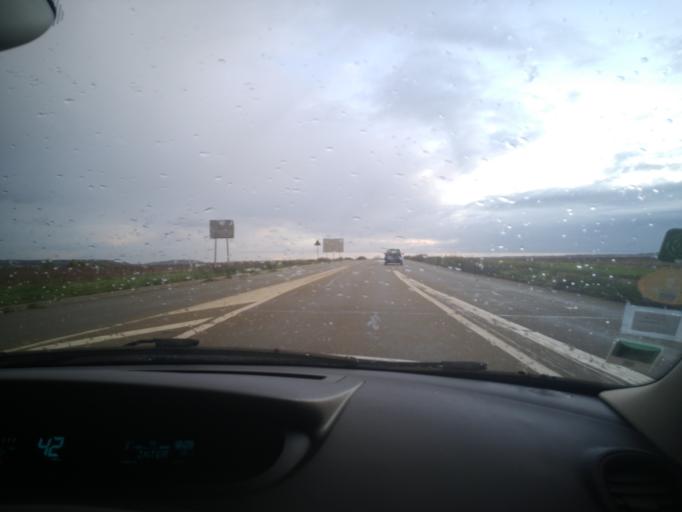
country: FR
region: Ile-de-France
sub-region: Departement des Yvelines
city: Plaisir
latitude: 48.8420
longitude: 1.9444
